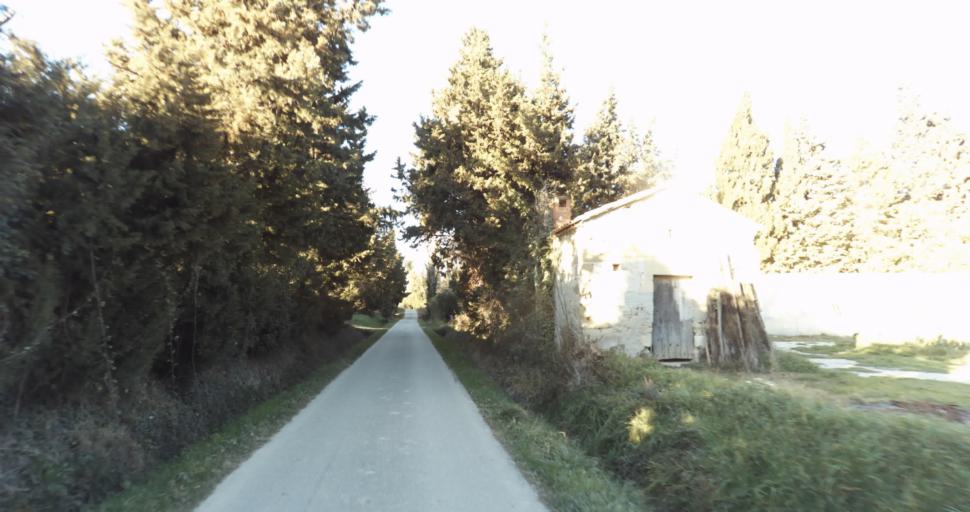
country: FR
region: Provence-Alpes-Cote d'Azur
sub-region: Departement des Bouches-du-Rhone
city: Barbentane
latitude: 43.9123
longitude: 4.7480
